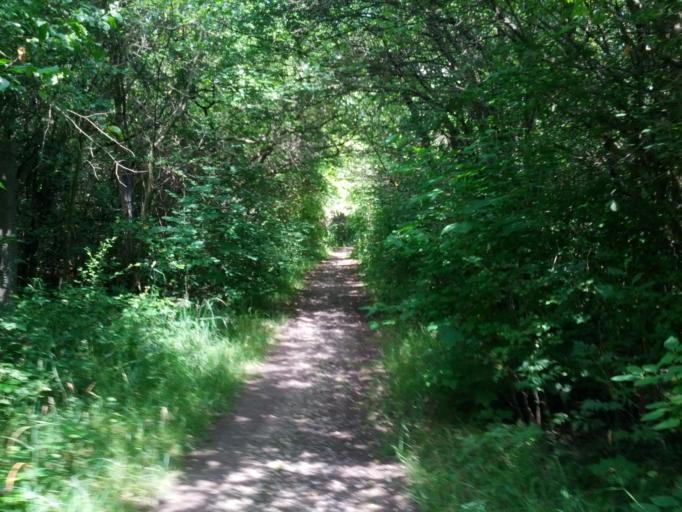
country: DE
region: Thuringia
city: Eisenach
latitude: 50.9913
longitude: 10.3520
